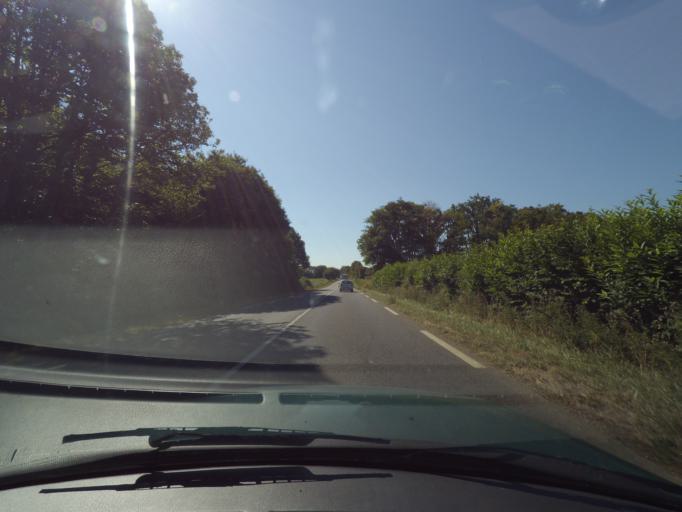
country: FR
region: Limousin
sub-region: Departement de la Haute-Vienne
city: Bussiere-Poitevine
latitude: 46.1877
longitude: 0.9317
